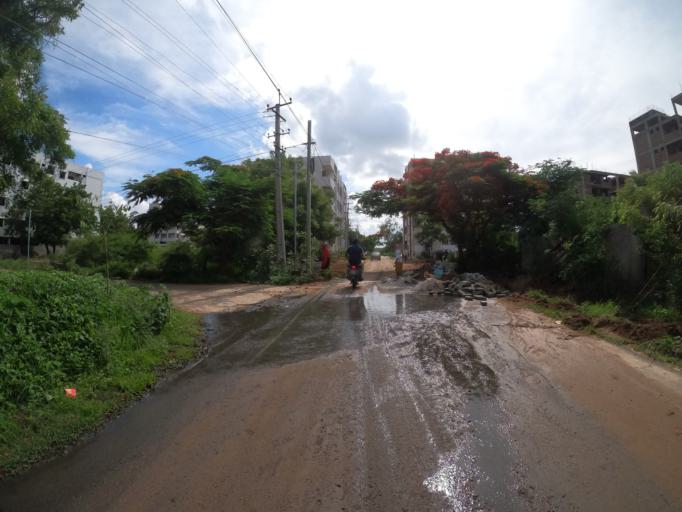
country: IN
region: Telangana
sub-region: Hyderabad
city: Hyderabad
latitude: 17.3542
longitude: 78.3964
